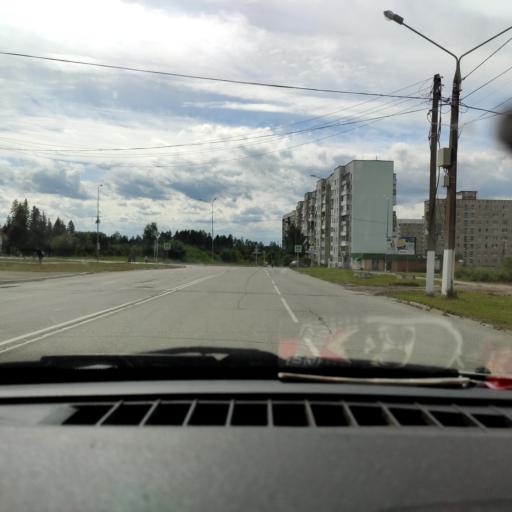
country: RU
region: Perm
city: Chusovoy
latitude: 58.2714
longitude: 57.8028
